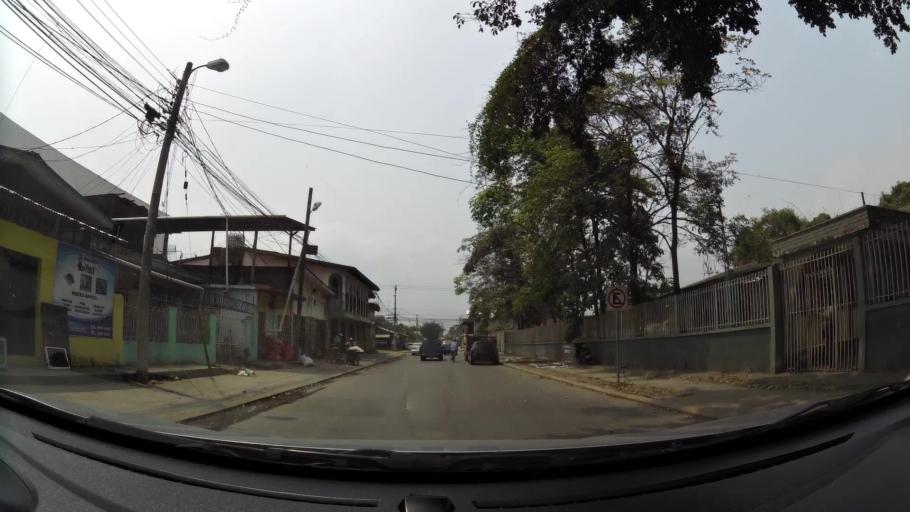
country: HN
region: Yoro
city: El Progreso
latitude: 15.4020
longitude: -87.8046
